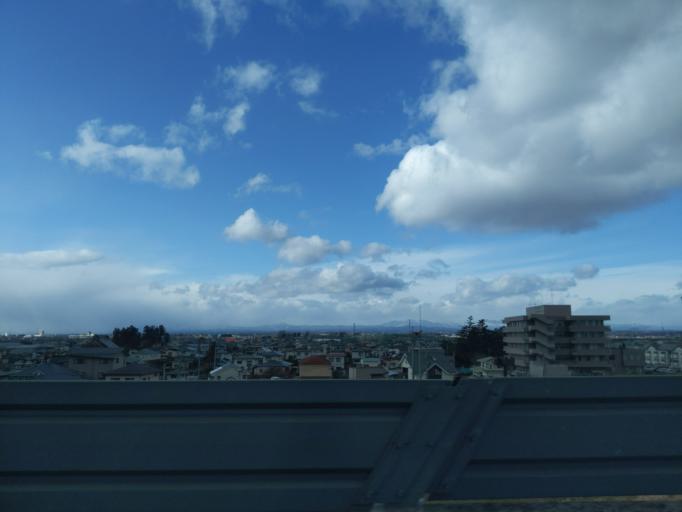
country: JP
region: Miyagi
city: Furukawa
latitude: 38.5875
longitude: 140.9735
